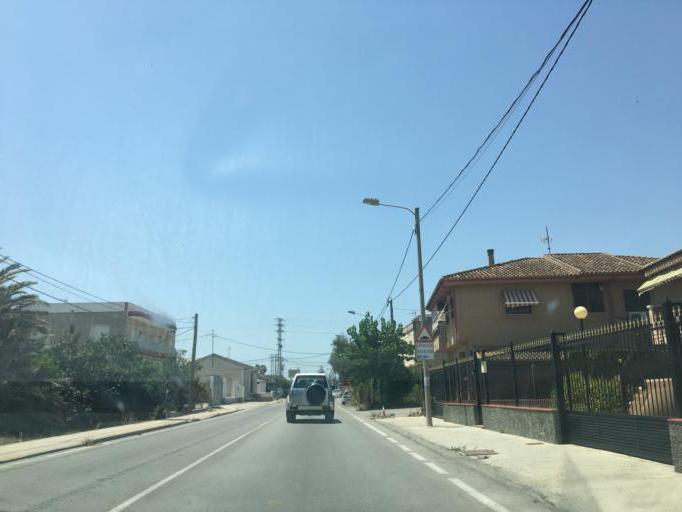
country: ES
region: Murcia
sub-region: Murcia
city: Murcia
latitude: 38.0109
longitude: -1.1086
